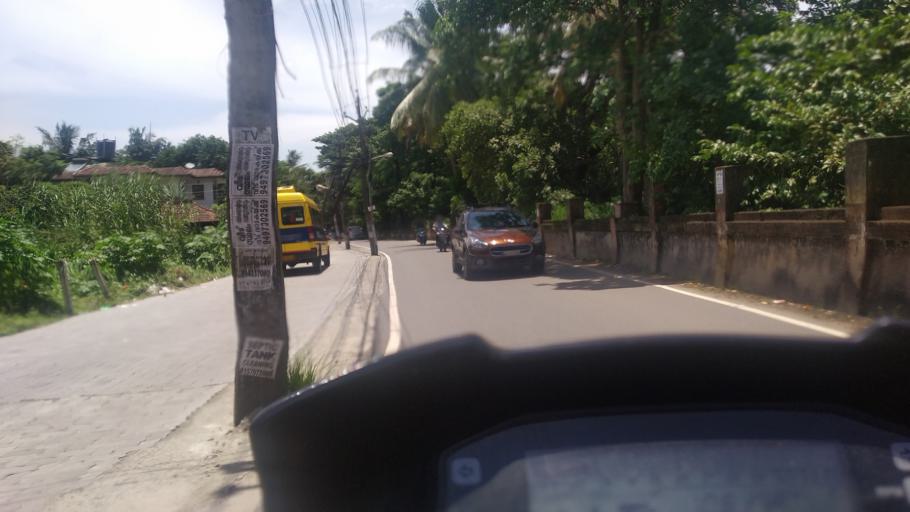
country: IN
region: Kerala
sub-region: Ernakulam
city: Cochin
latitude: 9.9709
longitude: 76.3050
